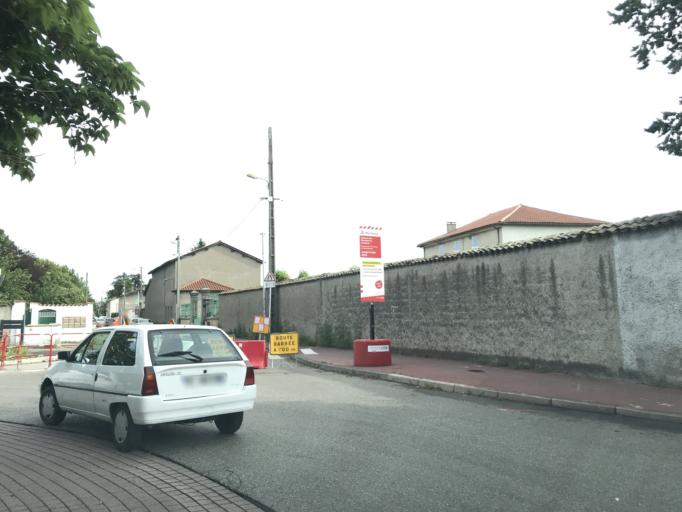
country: FR
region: Rhone-Alpes
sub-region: Departement du Rhone
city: Mions
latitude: 45.6695
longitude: 4.9587
